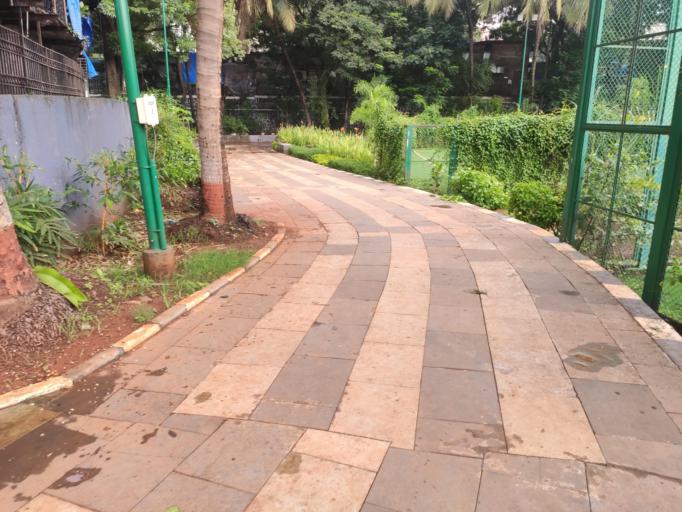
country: IN
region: Maharashtra
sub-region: Mumbai Suburban
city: Borivli
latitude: 19.2463
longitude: 72.8548
